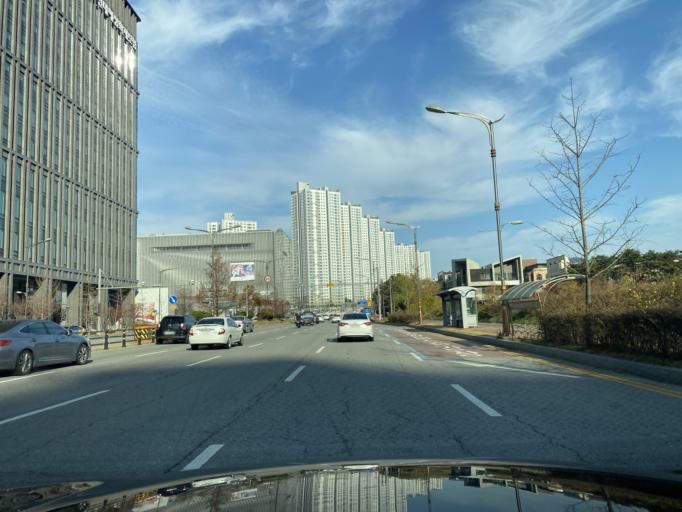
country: KR
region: Chungcheongnam-do
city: Cheonan
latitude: 36.7979
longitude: 127.1064
